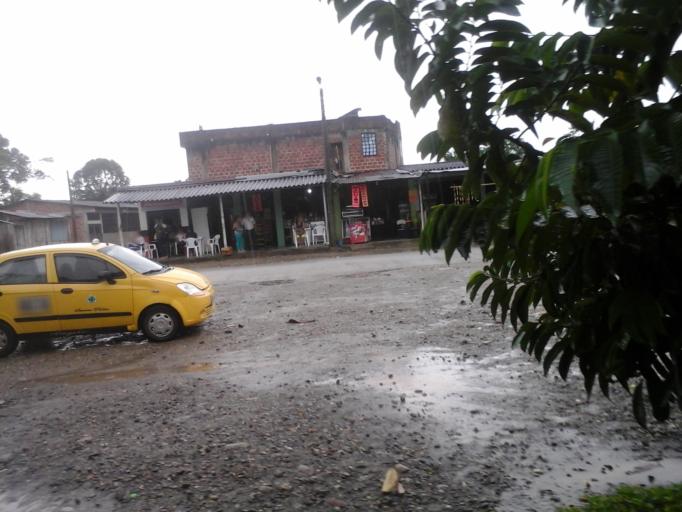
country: CO
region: Putumayo
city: Orito
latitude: 0.6475
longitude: -76.8248
